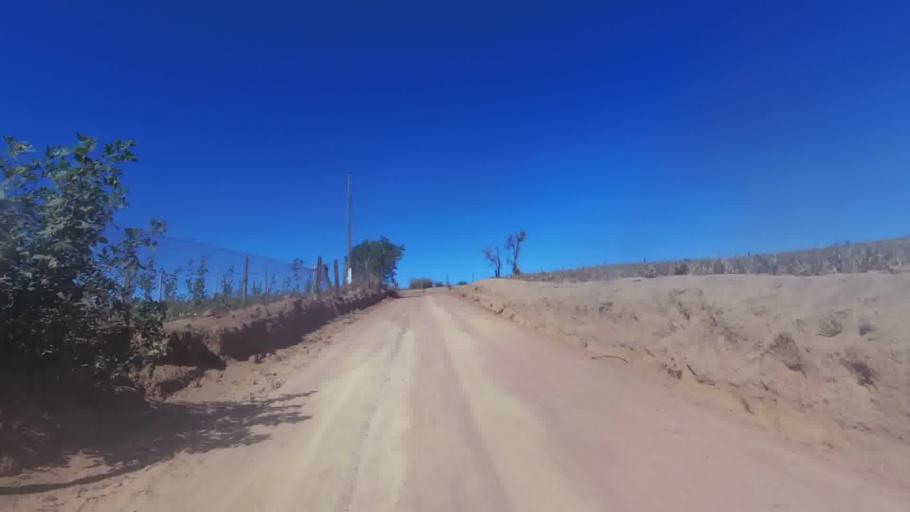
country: BR
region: Espirito Santo
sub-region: Marataizes
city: Marataizes
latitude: -21.1523
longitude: -40.9730
